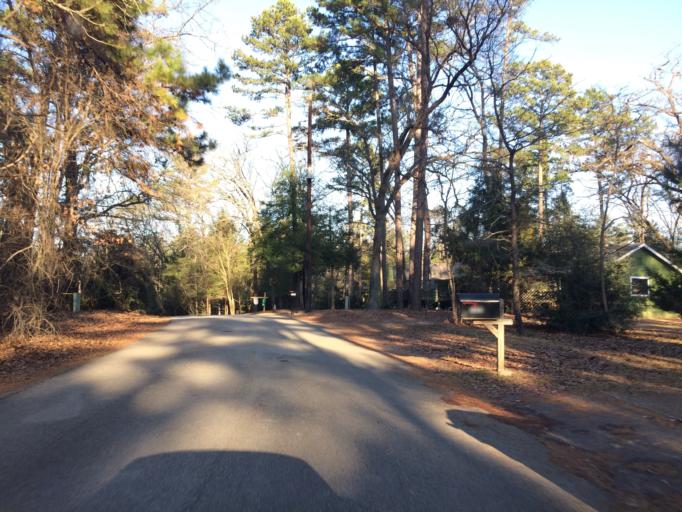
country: US
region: Texas
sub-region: Wood County
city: Hawkins
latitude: 32.7222
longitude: -95.1663
